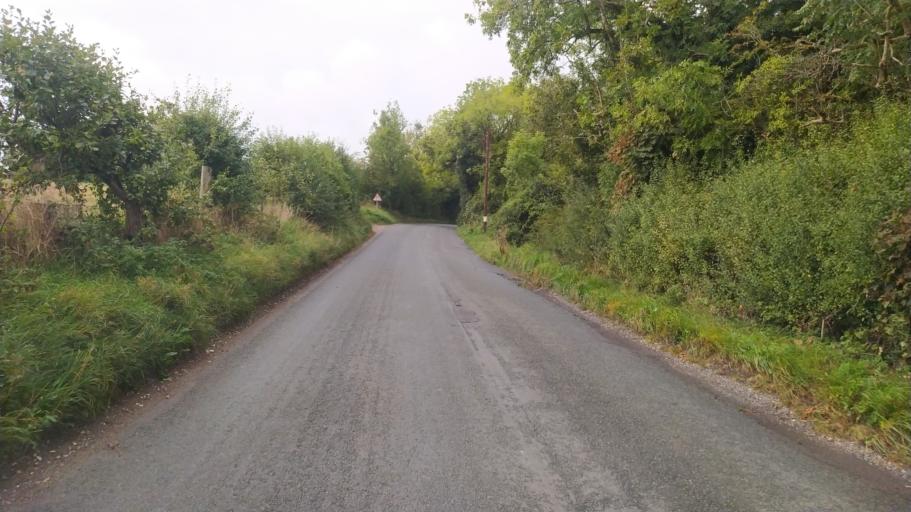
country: GB
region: England
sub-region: Wiltshire
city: Allington
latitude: 51.1240
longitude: -1.7343
